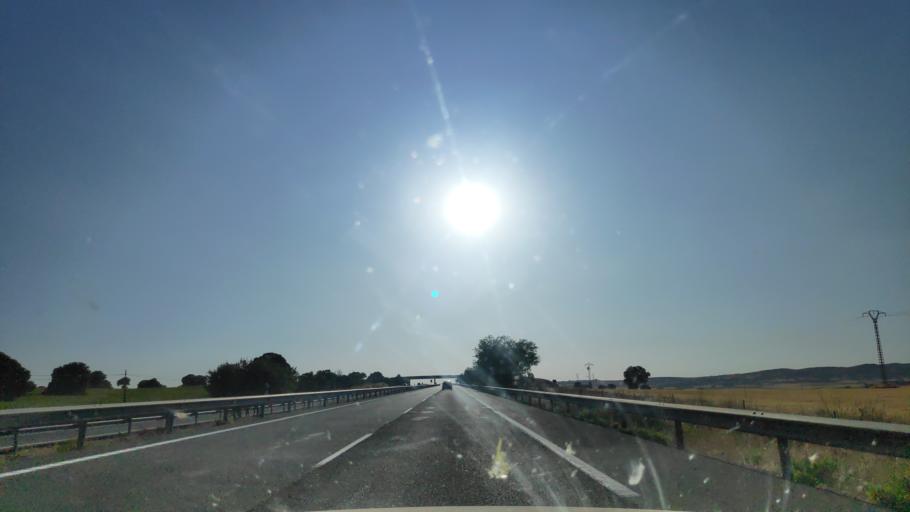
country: ES
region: Castille-La Mancha
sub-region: Provincia de Cuenca
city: Saelices
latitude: 39.9142
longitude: -2.7560
